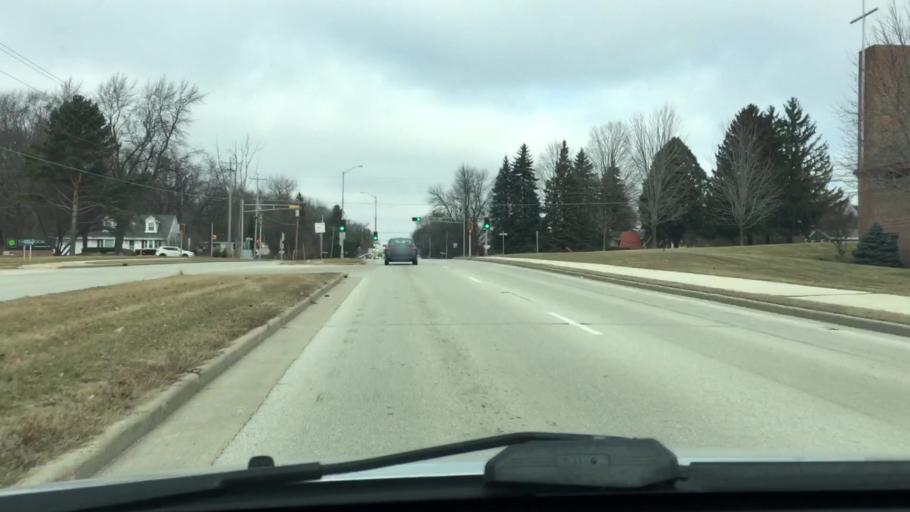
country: US
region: Wisconsin
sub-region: Waukesha County
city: Waukesha
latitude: 43.0237
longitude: -88.1667
